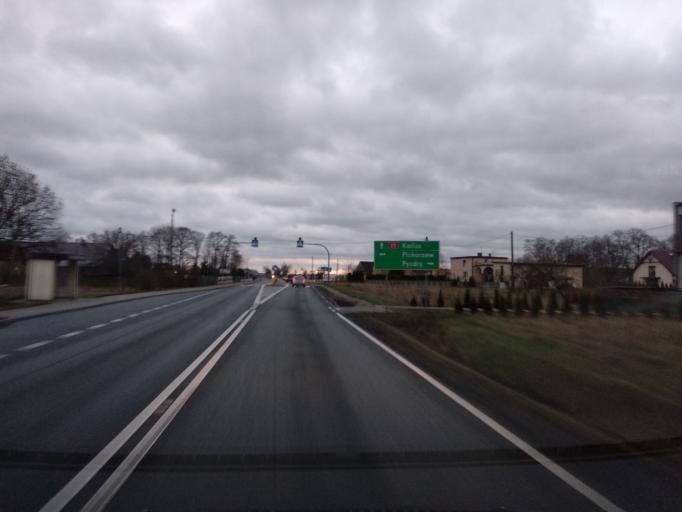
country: PL
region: Greater Poland Voivodeship
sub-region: Powiat koninski
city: Rychwal
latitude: 52.0965
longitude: 18.1669
